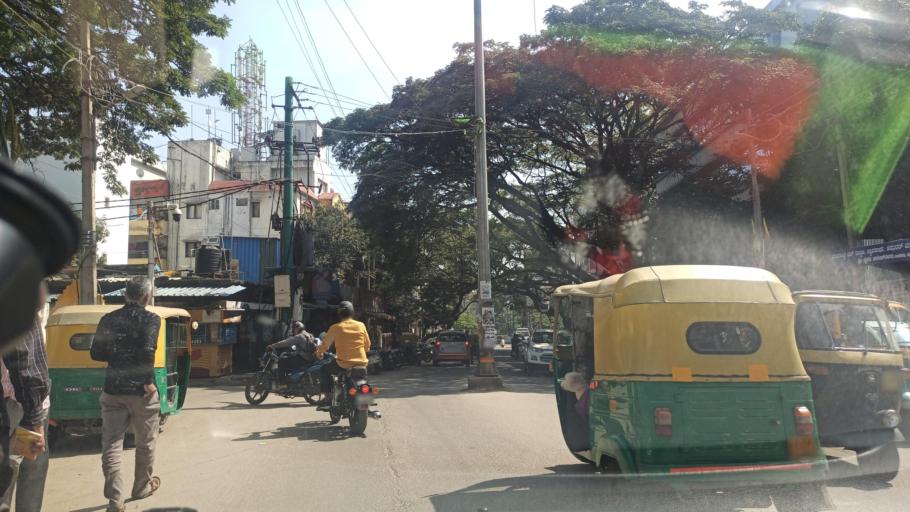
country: IN
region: Karnataka
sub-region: Bangalore Urban
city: Yelahanka
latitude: 13.0425
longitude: 77.5807
